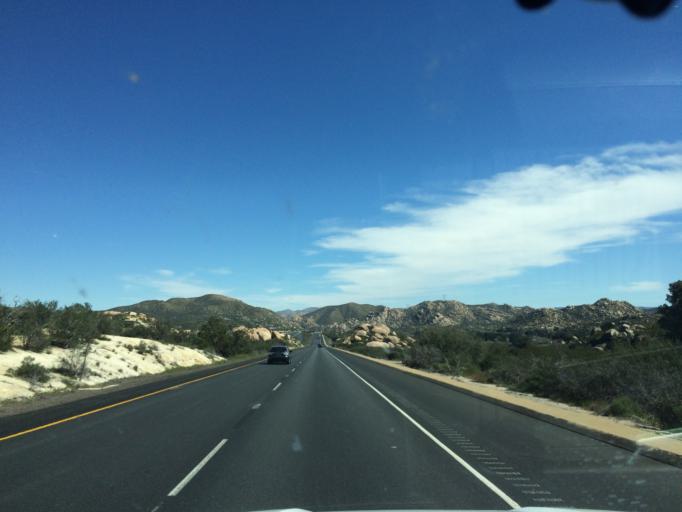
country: MX
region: Baja California
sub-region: Tecate
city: Cereso del Hongo
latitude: 32.6710
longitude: -116.2715
